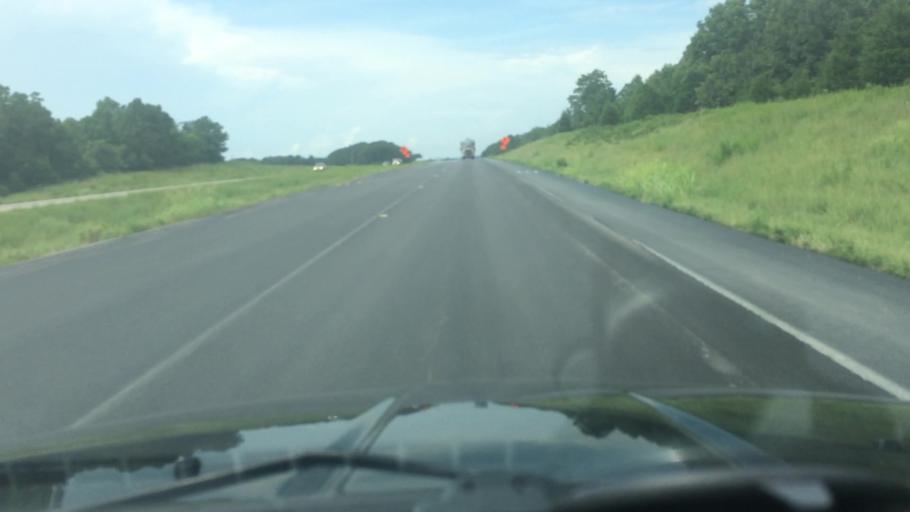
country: US
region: Missouri
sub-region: Saint Clair County
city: Osceola
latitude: 37.9644
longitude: -93.6444
